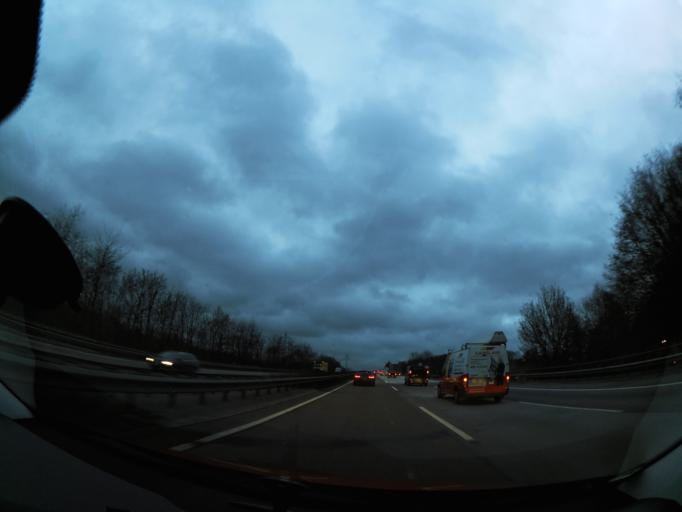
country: DE
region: Rheinland-Pfalz
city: Grossholbach
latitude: 50.4545
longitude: 7.8839
